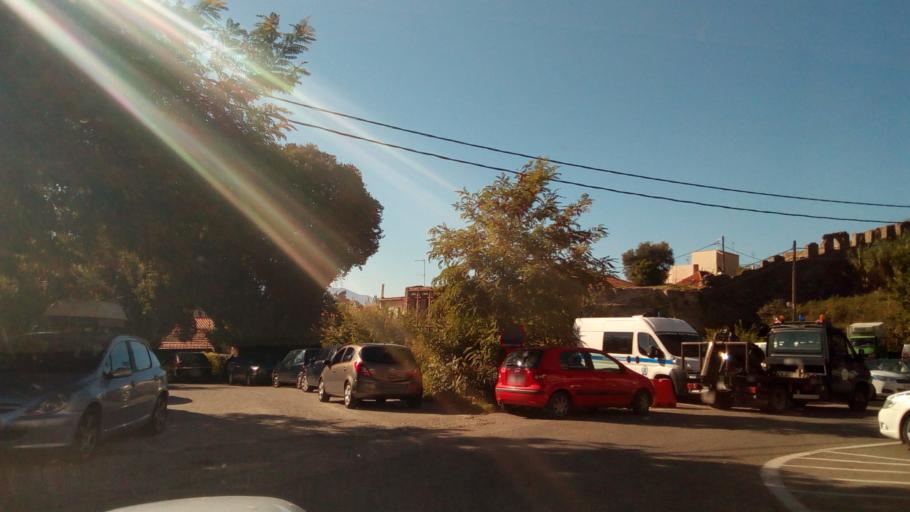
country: GR
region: West Greece
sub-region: Nomos Aitolias kai Akarnanias
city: Nafpaktos
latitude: 38.3947
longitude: 21.8303
